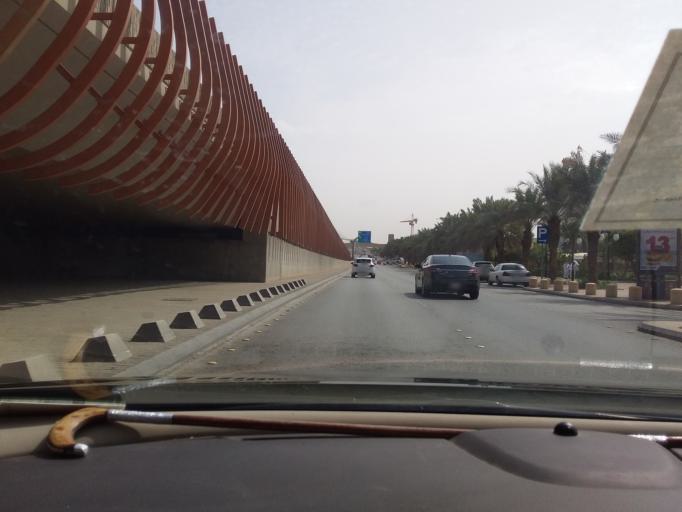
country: SA
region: Ar Riyad
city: Riyadh
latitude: 24.7422
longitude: 46.7039
